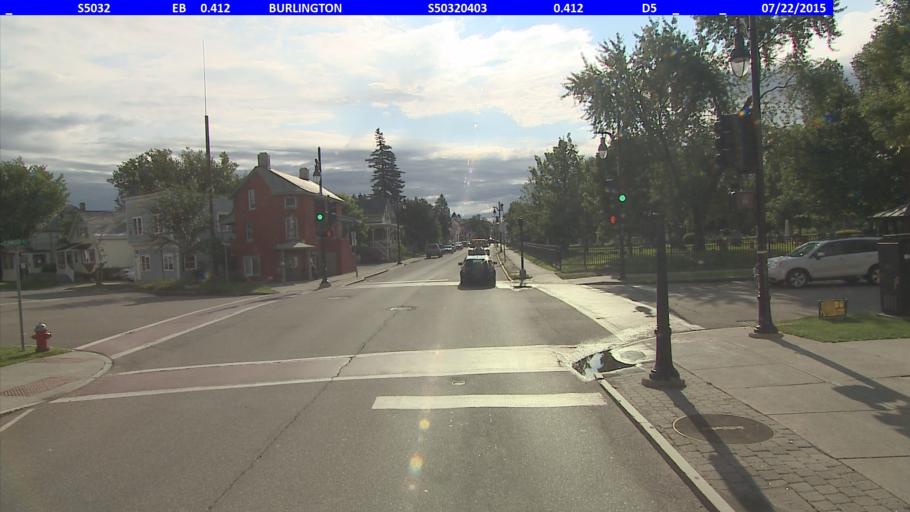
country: US
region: Vermont
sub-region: Chittenden County
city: Burlington
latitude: 44.4847
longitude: -73.2141
